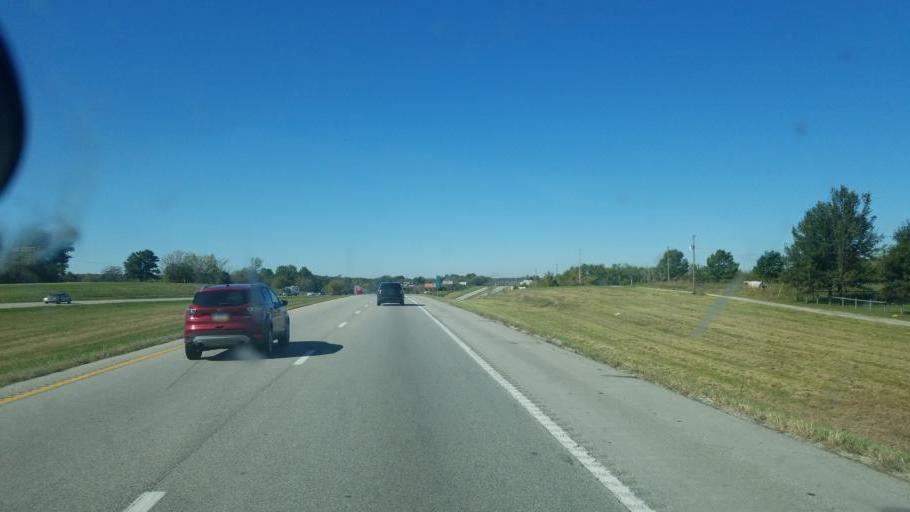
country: US
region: Missouri
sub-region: Jackson County
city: Oak Grove
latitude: 39.0169
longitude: -94.1535
